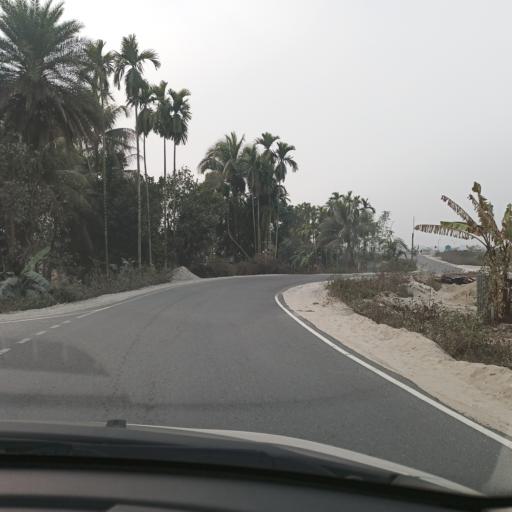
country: IN
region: West Bengal
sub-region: Jalpaiguri
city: Odlabari
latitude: 26.7448
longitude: 88.5801
